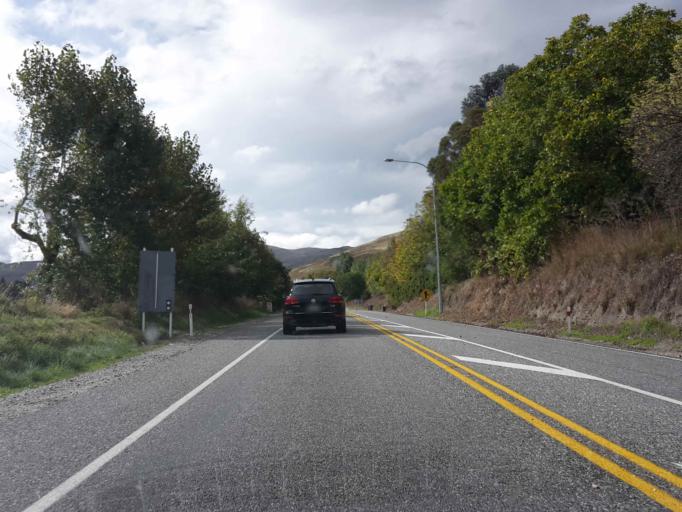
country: NZ
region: Otago
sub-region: Queenstown-Lakes District
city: Arrowtown
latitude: -44.9872
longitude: 168.8158
